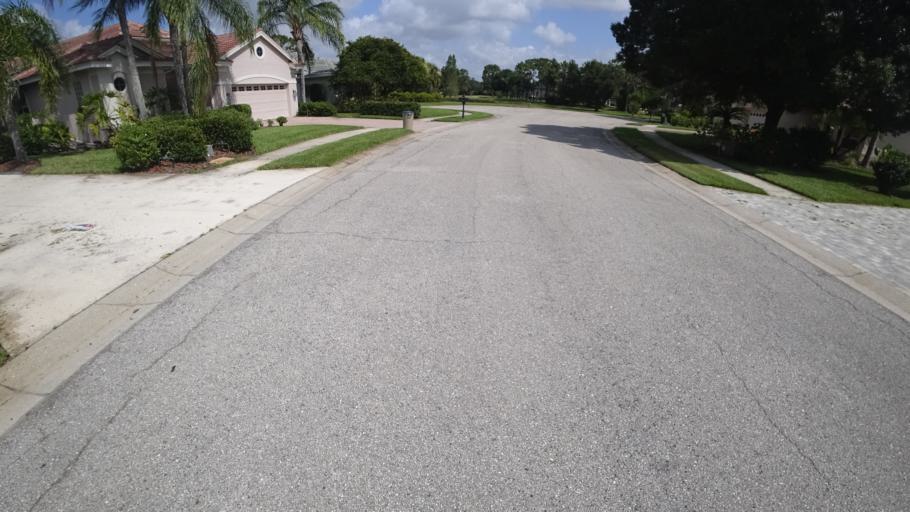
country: US
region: Florida
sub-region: Sarasota County
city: The Meadows
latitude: 27.4094
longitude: -82.4432
